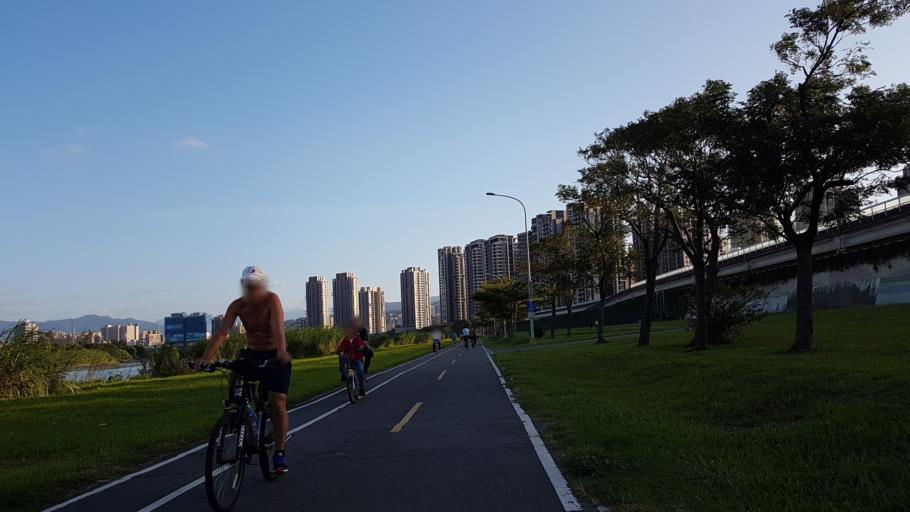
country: TW
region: Taipei
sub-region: Taipei
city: Banqiao
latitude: 25.0182
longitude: 121.4872
